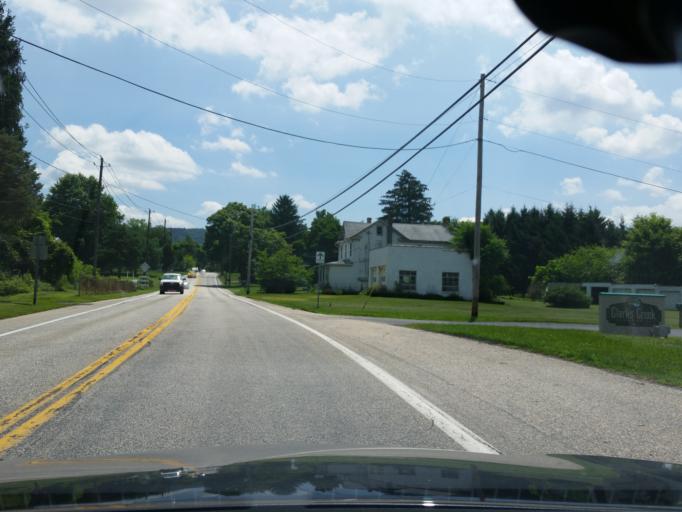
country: US
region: Pennsylvania
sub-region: Perry County
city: Marysville
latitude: 40.3870
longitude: -76.9411
